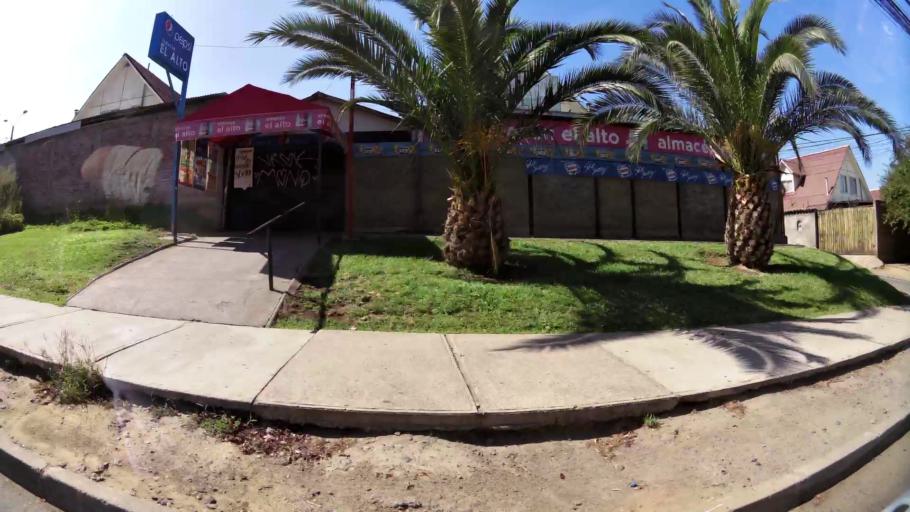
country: CL
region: Maule
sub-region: Provincia de Talca
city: Talca
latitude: -35.4089
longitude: -71.6438
